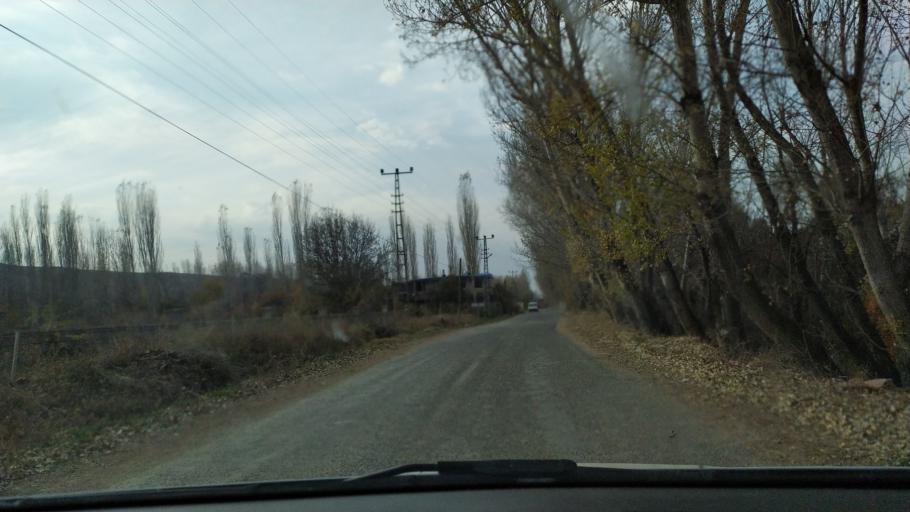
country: TR
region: Kayseri
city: Akkisla
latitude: 38.9956
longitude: 36.1180
